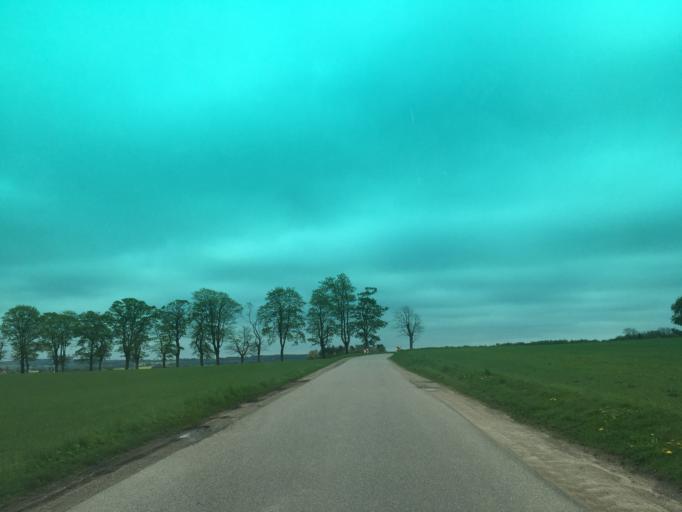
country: DK
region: Zealand
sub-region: Soro Kommune
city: Frederiksberg
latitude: 55.4037
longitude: 11.6569
